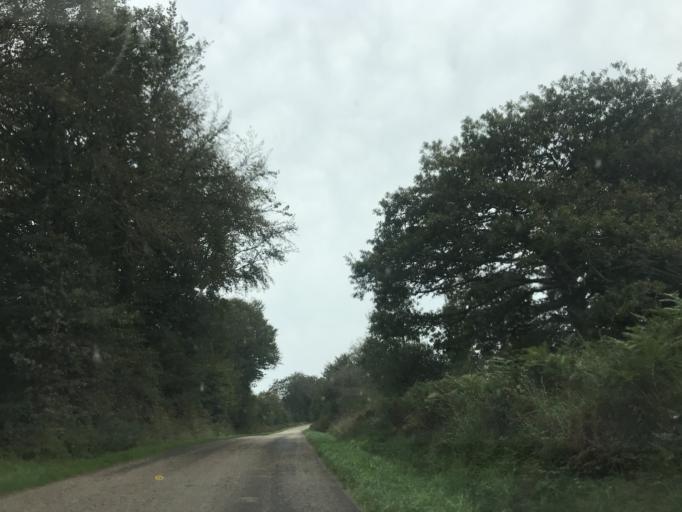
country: FR
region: Brittany
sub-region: Departement du Finistere
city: Plouneour-Menez
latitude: 48.3835
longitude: -3.8776
